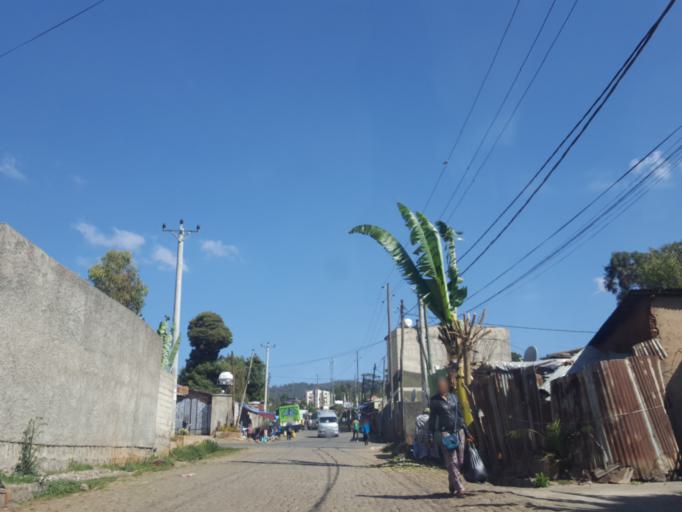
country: ET
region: Adis Abeba
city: Addis Ababa
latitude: 9.0595
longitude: 38.7332
